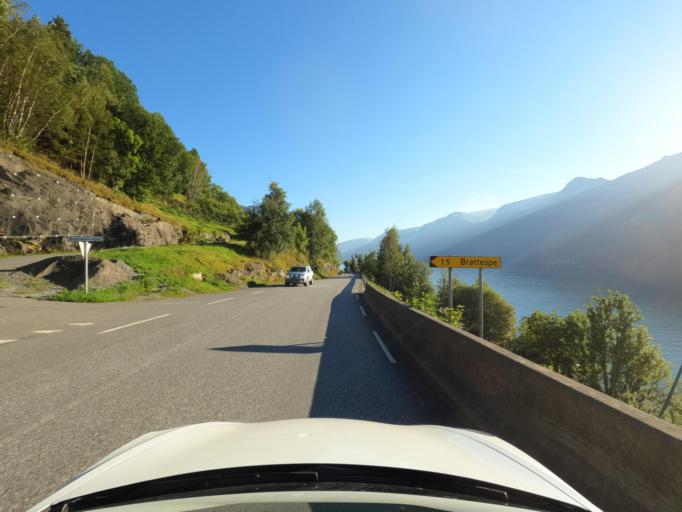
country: NO
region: Hordaland
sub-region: Odda
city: Odda
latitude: 60.2190
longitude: 6.6033
